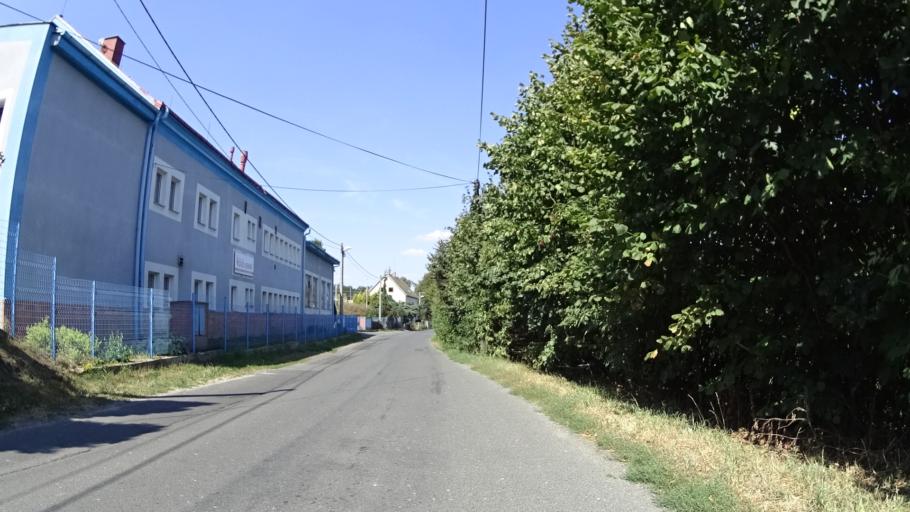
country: CZ
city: Hradek nad Nisou
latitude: 50.8380
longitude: 14.8623
